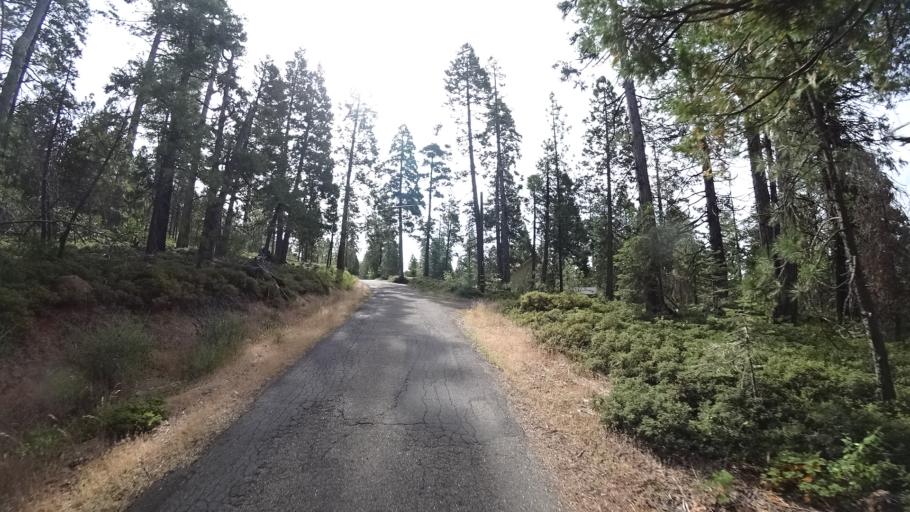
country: US
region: California
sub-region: Calaveras County
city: Arnold
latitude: 38.2666
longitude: -120.3244
